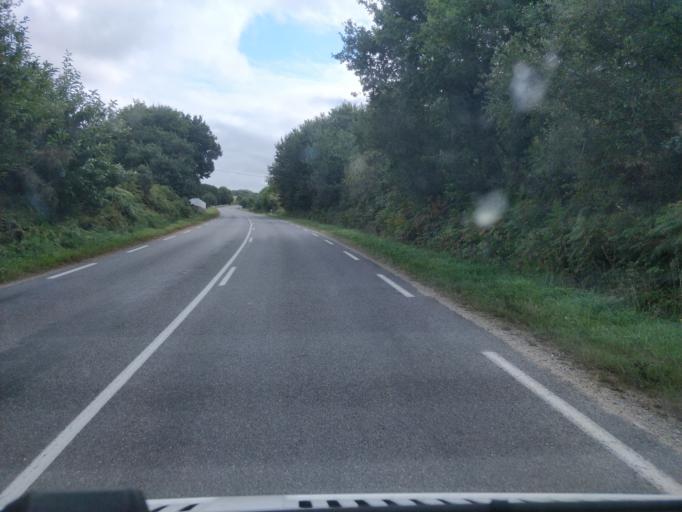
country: FR
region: Brittany
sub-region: Departement du Finistere
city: Plogastel-Saint-Germain
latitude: 47.9952
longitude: -4.2478
